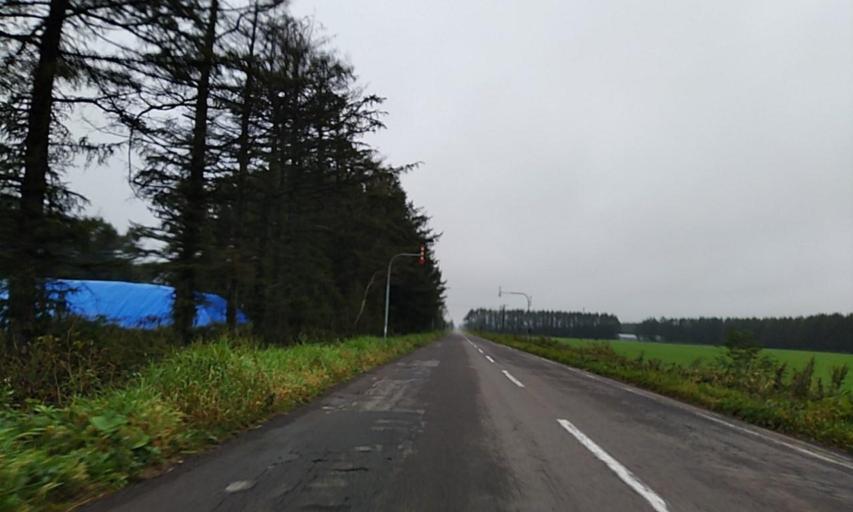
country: JP
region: Hokkaido
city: Shibetsu
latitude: 43.5161
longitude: 144.6785
